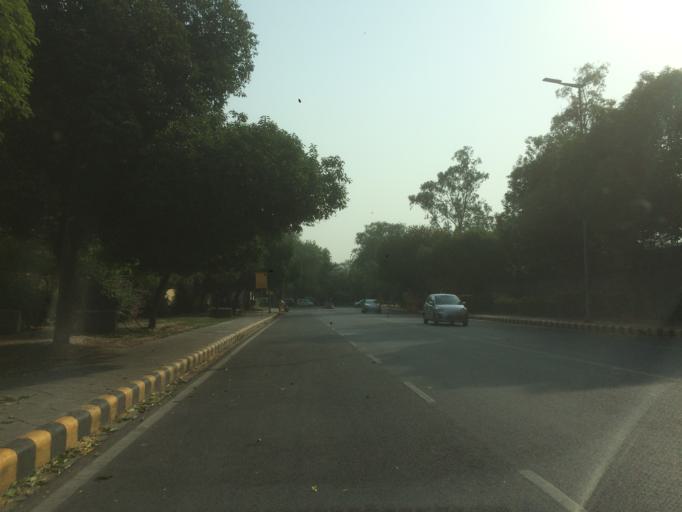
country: IN
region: NCT
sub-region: Central Delhi
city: Karol Bagh
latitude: 28.5999
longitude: 77.1813
